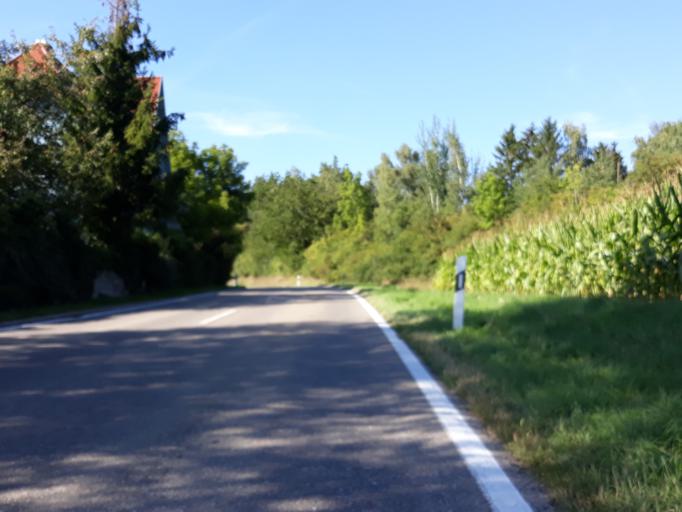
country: DE
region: Baden-Wuerttemberg
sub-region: Regierungsbezirk Stuttgart
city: Weil der Stadt
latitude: 48.7231
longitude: 8.8773
